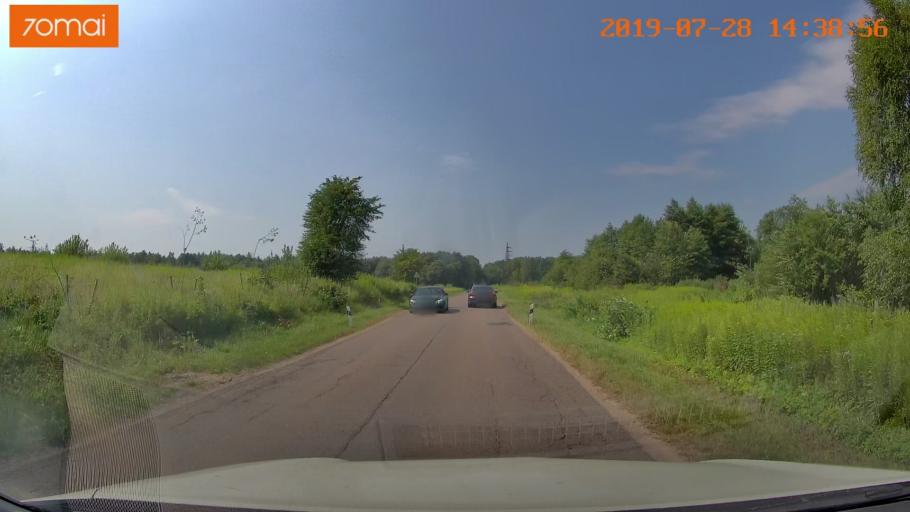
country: RU
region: Kaliningrad
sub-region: Gorod Kaliningrad
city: Yantarnyy
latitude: 54.8463
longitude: 19.9769
